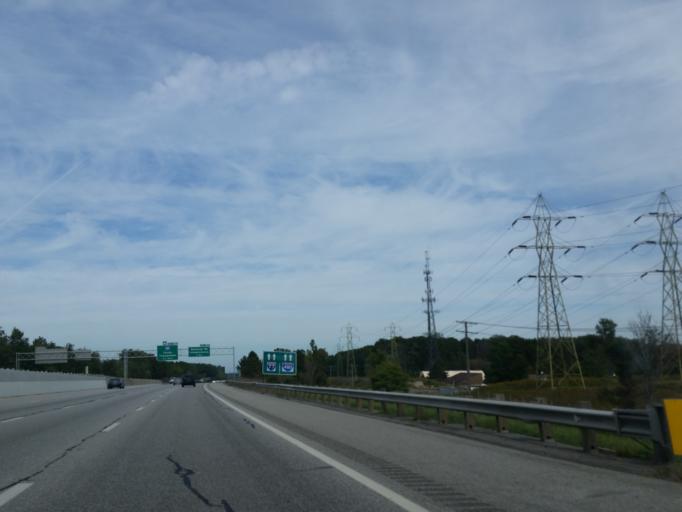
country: US
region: Ohio
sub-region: Cuyahoga County
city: Independence
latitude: 41.3742
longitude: -81.6522
